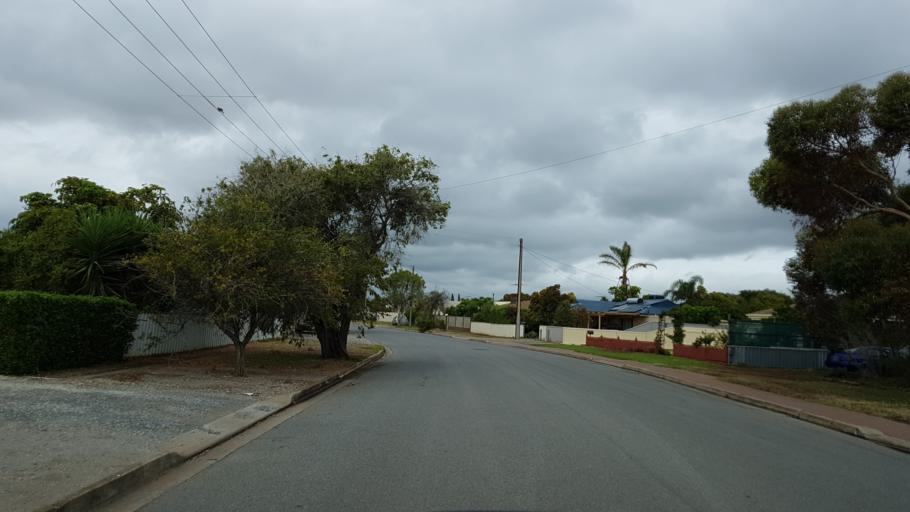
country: AU
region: South Australia
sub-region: Onkaparinga
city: Port Willunga
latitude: -35.2770
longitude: 138.4469
